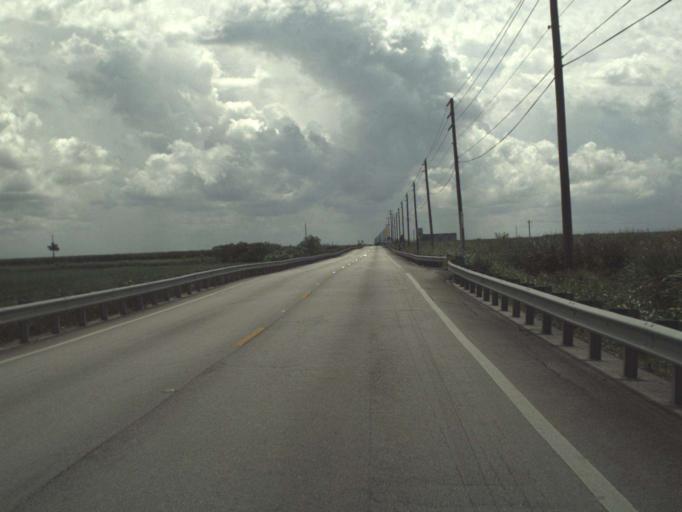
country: US
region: Florida
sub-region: Palm Beach County
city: Pahokee
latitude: 26.7880
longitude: -80.6534
